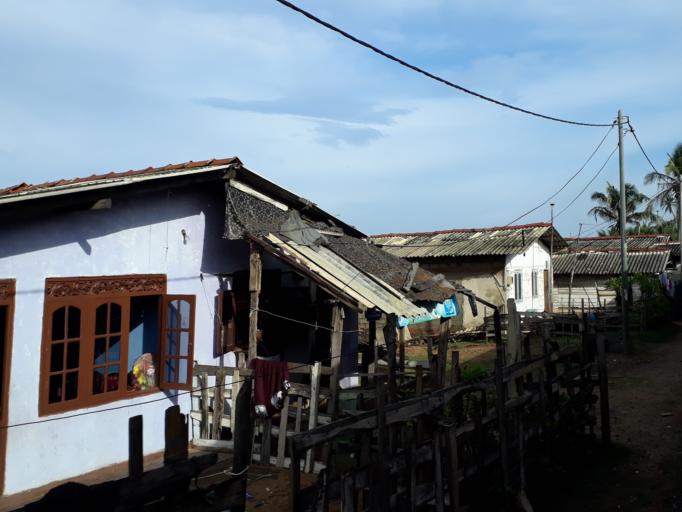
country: LK
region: Western
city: Moratuwa
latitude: 6.7855
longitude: 79.8758
